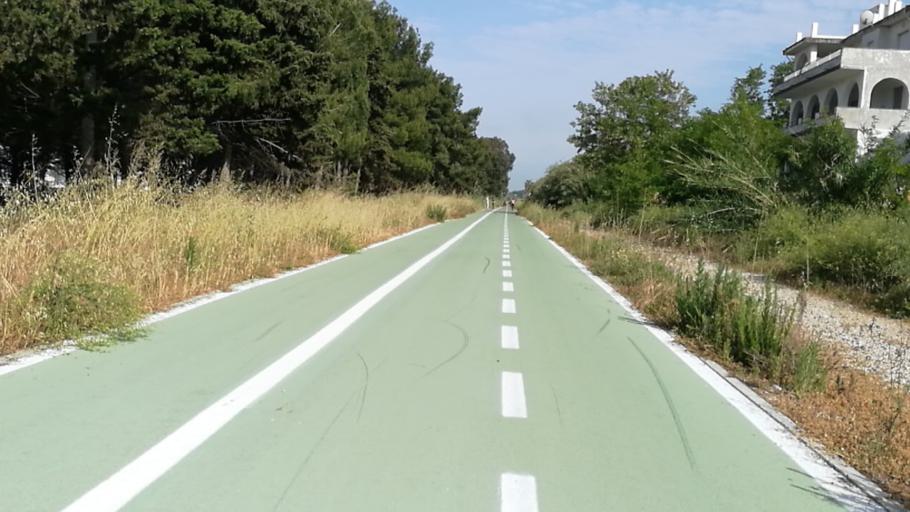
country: IT
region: Abruzzo
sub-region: Provincia di Chieti
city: Casalbordino-Miracoli
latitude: 42.2070
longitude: 14.5986
